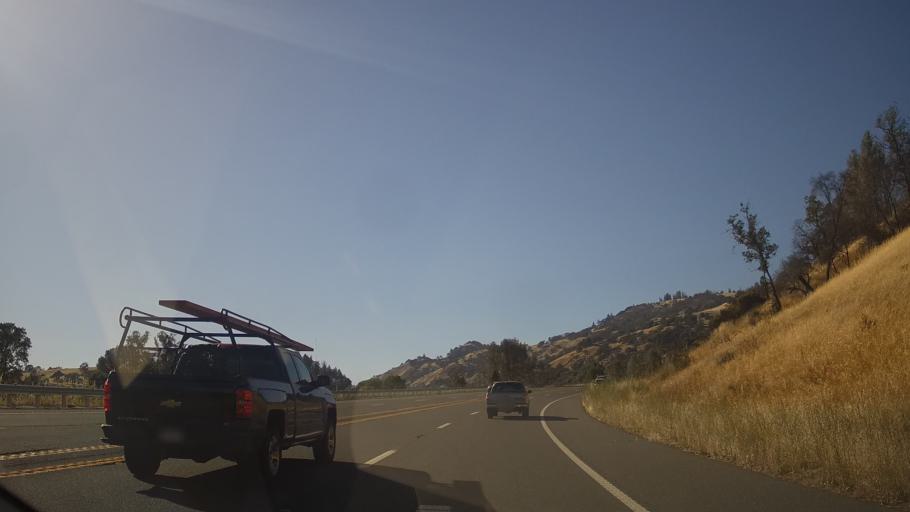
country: US
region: California
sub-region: Mendocino County
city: Redwood Valley
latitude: 39.2779
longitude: -123.2573
